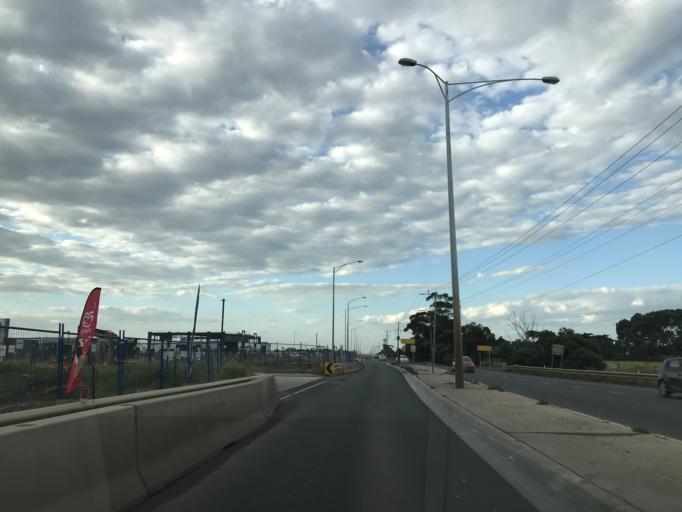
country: AU
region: Victoria
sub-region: Wyndham
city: Truganina
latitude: -37.8385
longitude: 144.7471
